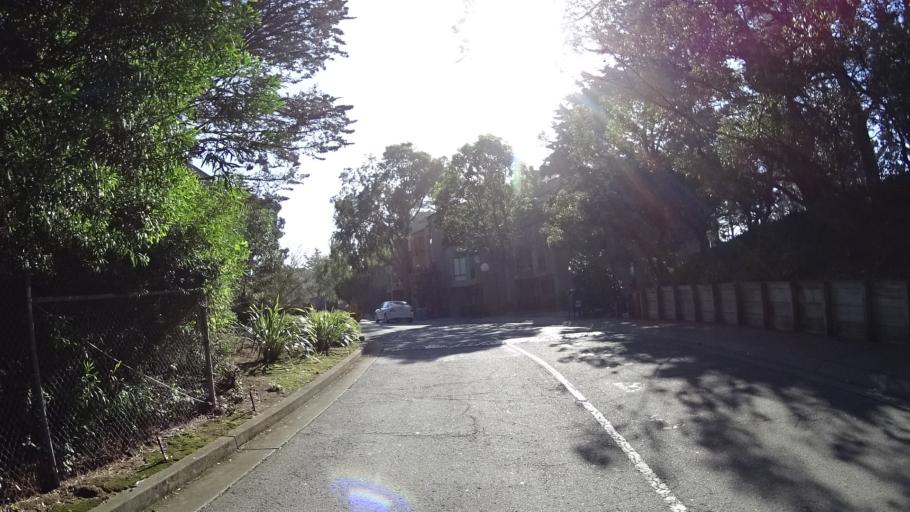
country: US
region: California
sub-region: San Mateo County
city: Daly City
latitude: 37.7109
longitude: -122.4839
